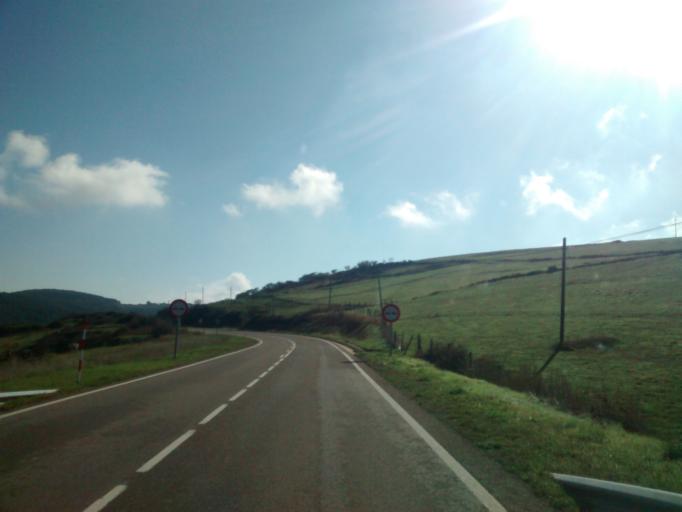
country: ES
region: Cantabria
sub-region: Provincia de Cantabria
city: Reinosa
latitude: 42.9900
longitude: -4.1140
